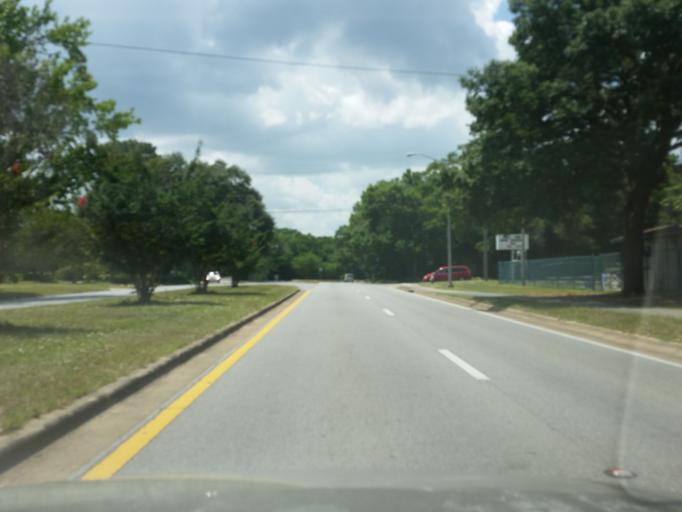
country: US
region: Florida
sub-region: Escambia County
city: Goulding
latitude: 30.4663
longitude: -87.1987
